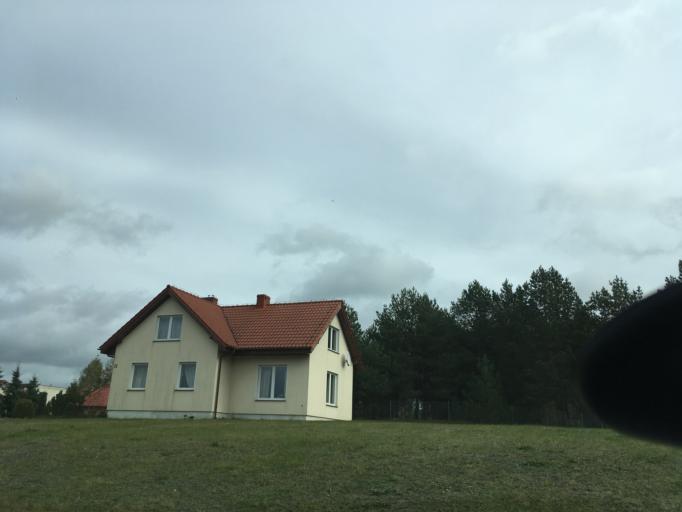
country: PL
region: Pomeranian Voivodeship
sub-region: Powiat koscierski
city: Koscierzyna
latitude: 54.1072
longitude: 18.0080
